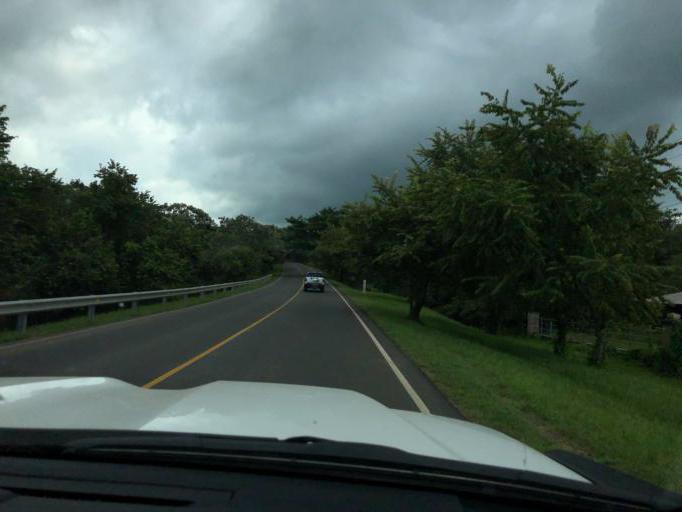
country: NI
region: Chontales
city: Villa Sandino
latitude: 12.0544
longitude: -85.0304
